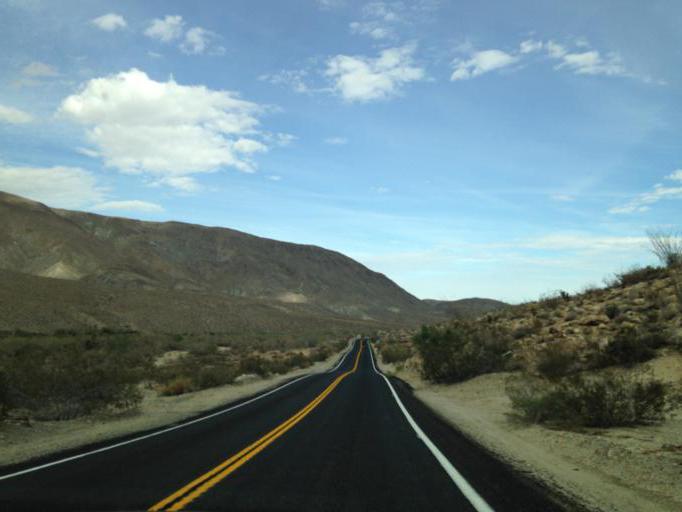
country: US
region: California
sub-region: San Diego County
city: Borrego Springs
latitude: 33.1337
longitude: -116.3920
